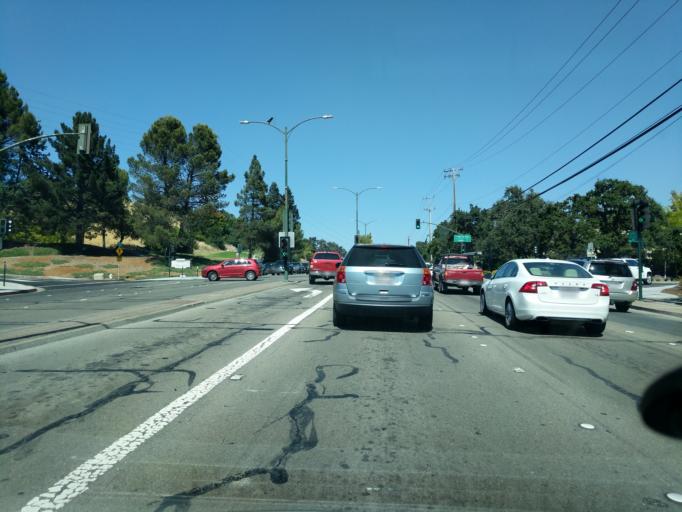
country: US
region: California
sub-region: Contra Costa County
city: Waldon
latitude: 37.9112
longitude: -122.0466
